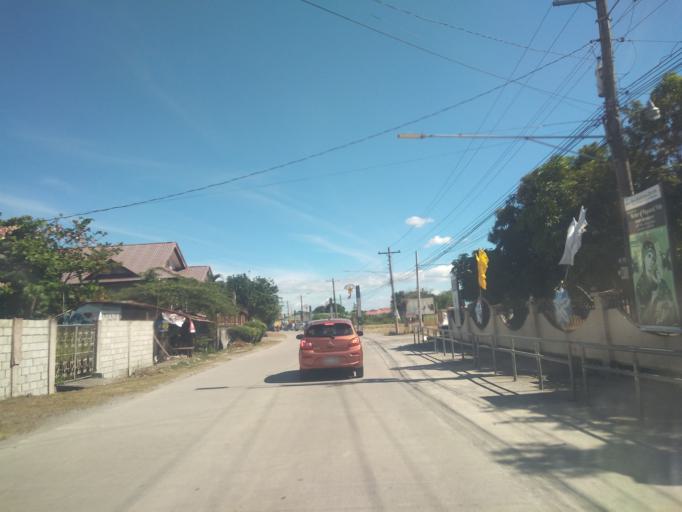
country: PH
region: Central Luzon
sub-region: Province of Pampanga
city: Bacolor
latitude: 15.0008
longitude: 120.6489
